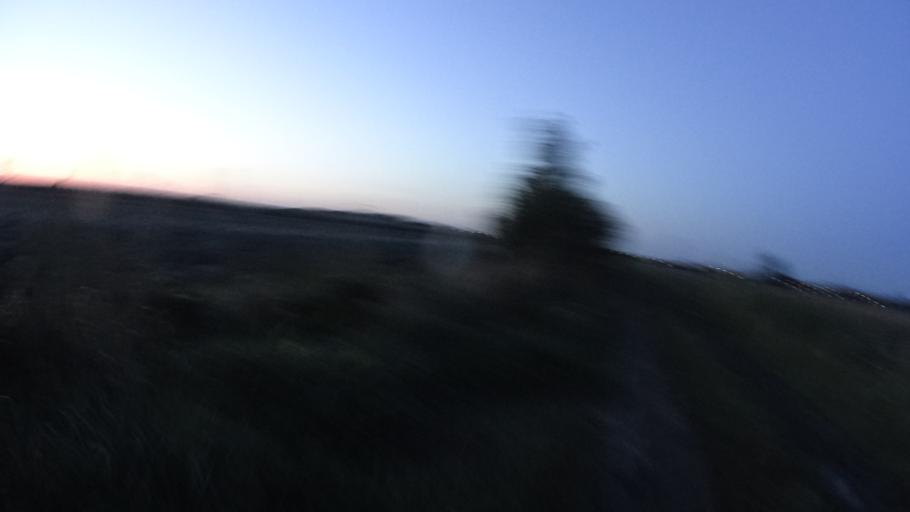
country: PL
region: Masovian Voivodeship
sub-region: Powiat warszawski zachodni
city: Ozarow Mazowiecki
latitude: 52.2238
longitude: 20.7911
